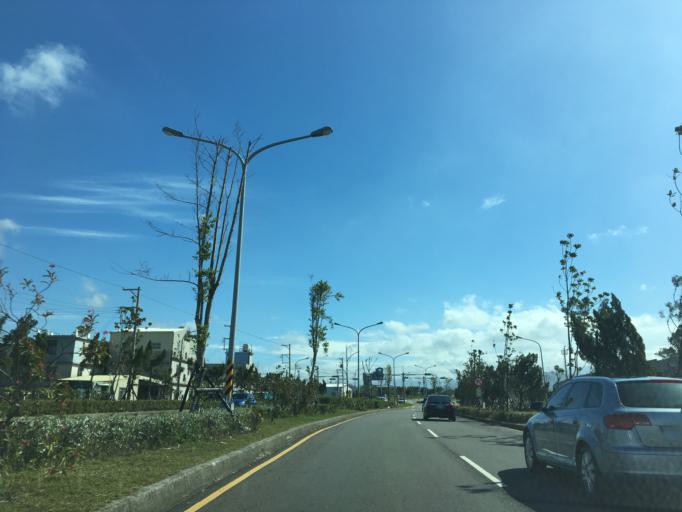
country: TW
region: Taiwan
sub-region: Hsinchu
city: Zhubei
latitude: 24.7818
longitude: 121.0482
